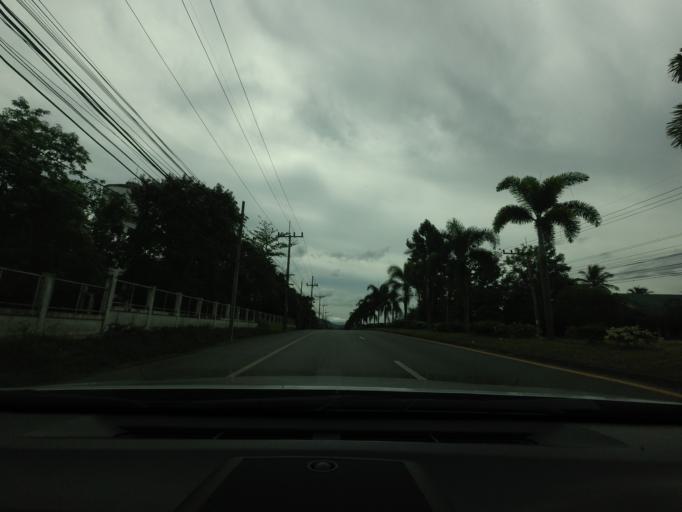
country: TH
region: Songkhla
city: Sadao
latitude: 6.6567
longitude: 100.3371
